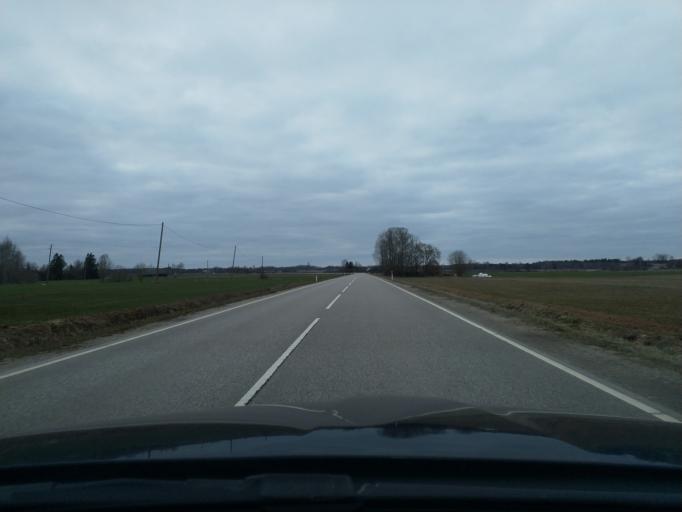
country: LV
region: Talsu Rajons
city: Sabile
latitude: 56.9320
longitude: 22.5200
